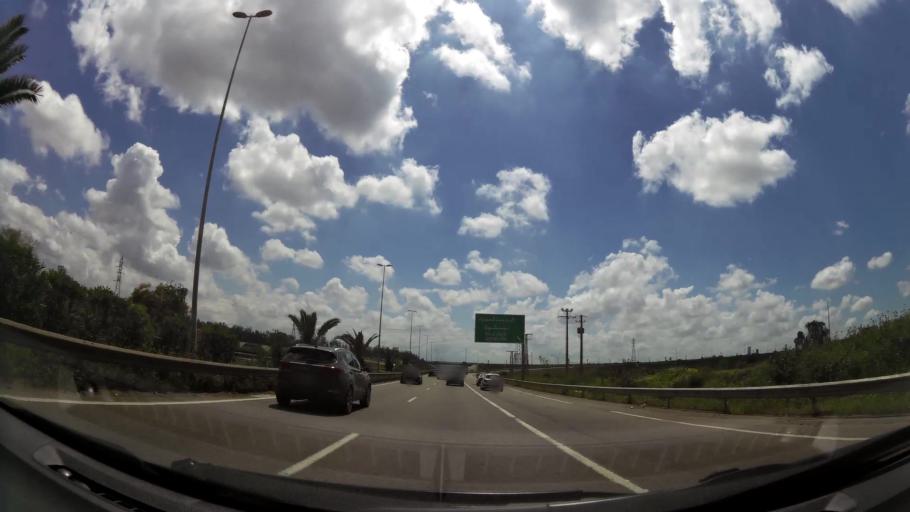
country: MA
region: Grand Casablanca
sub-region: Nouaceur
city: Bouskoura
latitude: 33.4860
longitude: -7.6319
